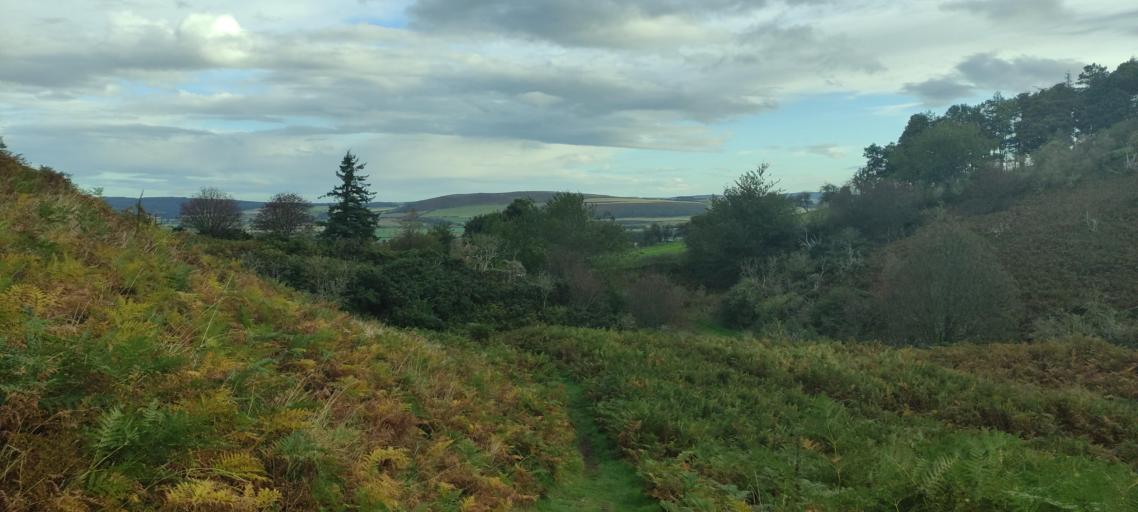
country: GB
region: England
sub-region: Northumberland
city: Wooler
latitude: 55.5415
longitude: -2.0266
